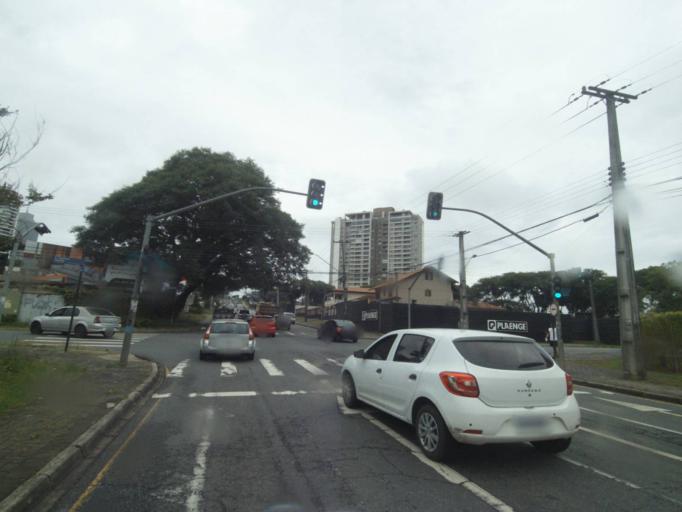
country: BR
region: Parana
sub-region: Curitiba
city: Curitiba
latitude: -25.4358
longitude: -49.3135
